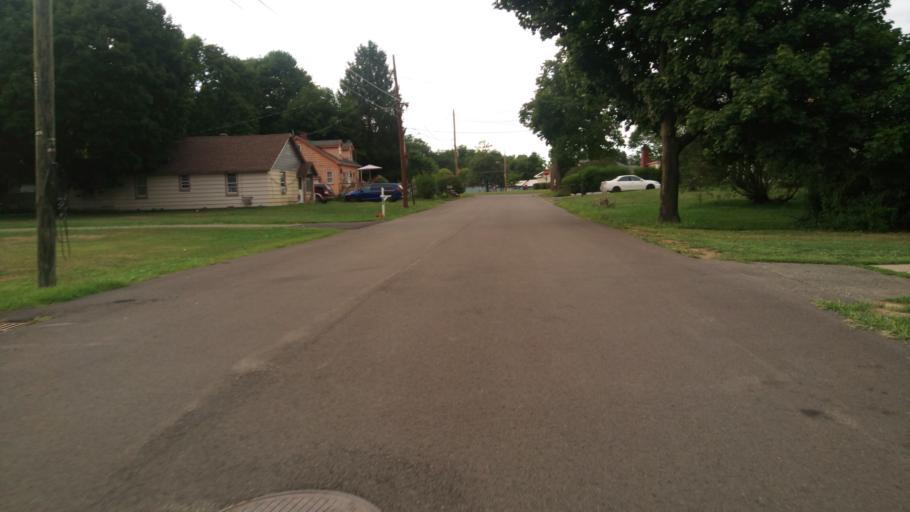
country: US
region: New York
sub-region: Chemung County
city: Southport
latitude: 42.0608
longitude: -76.8162
